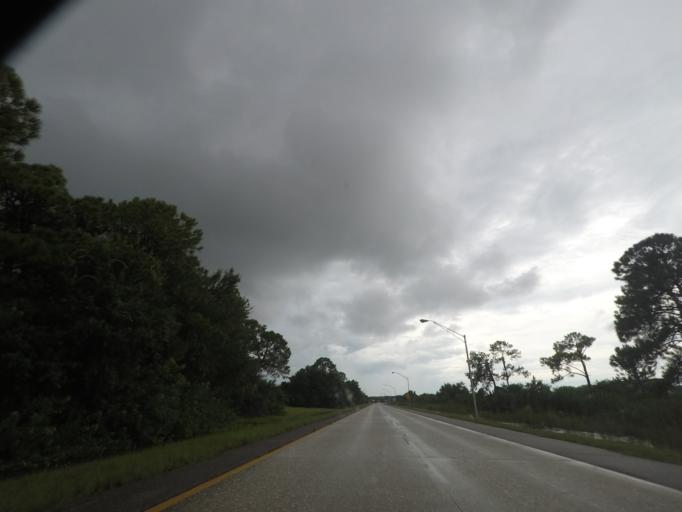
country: US
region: Florida
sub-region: Pinellas County
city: Pinellas Park
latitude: 27.8545
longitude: -82.6655
